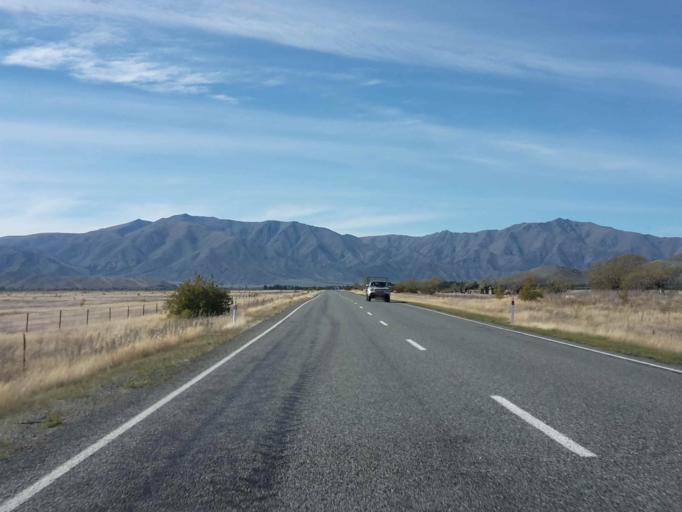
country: NZ
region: Otago
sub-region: Queenstown-Lakes District
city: Wanaka
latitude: -44.5001
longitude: 169.9016
